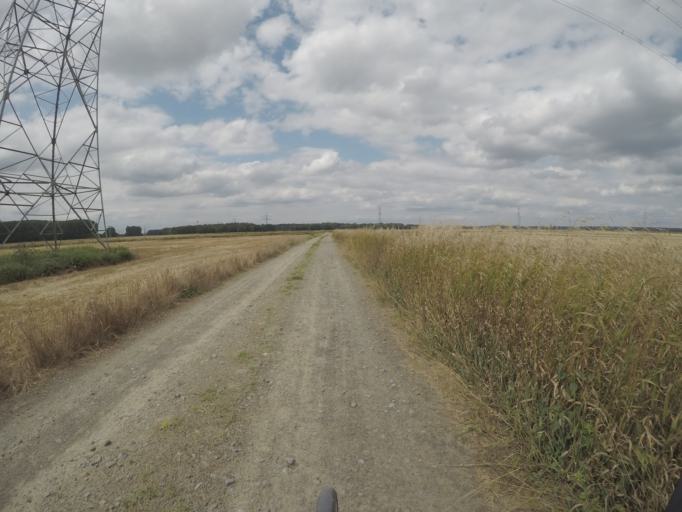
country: DE
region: Brandenburg
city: Brieselang
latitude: 52.6123
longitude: 13.0540
